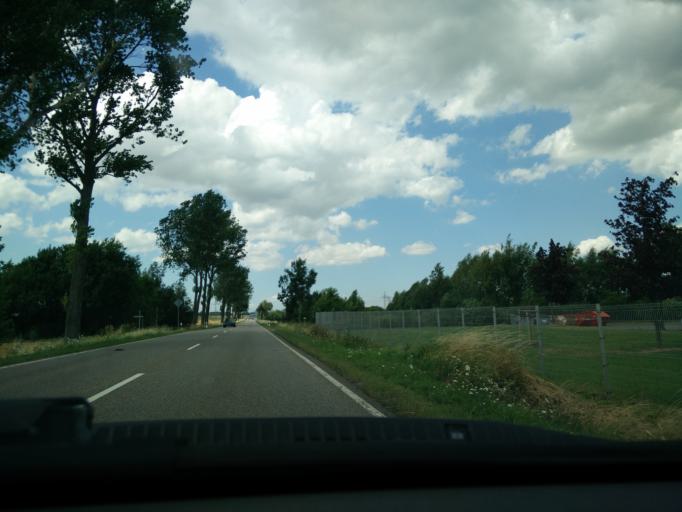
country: DE
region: Saxony
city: Wittgensdorf
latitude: 50.8661
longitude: 12.8480
